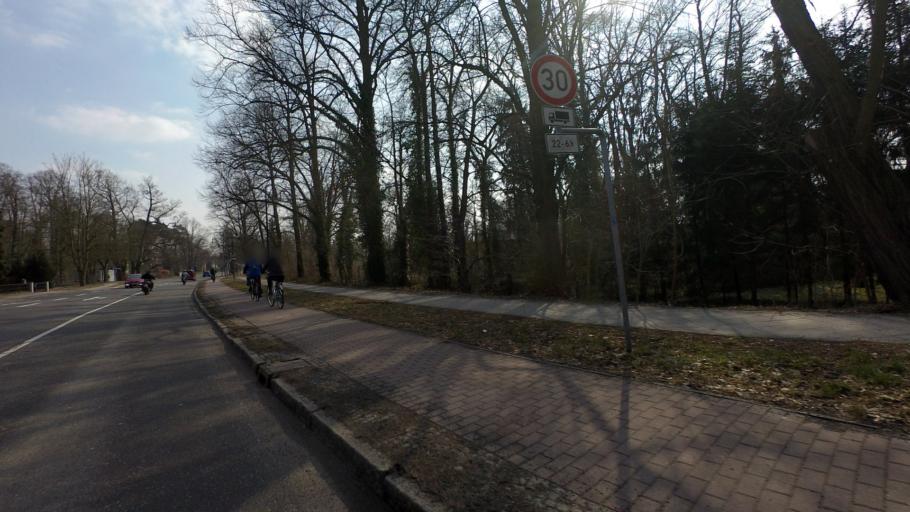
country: DE
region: Brandenburg
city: Potsdam
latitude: 52.3550
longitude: 13.1026
